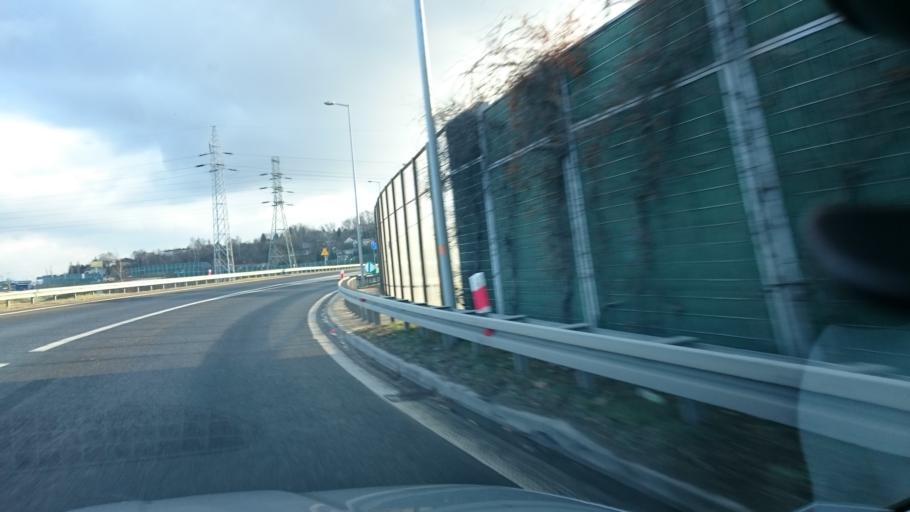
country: PL
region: Lesser Poland Voivodeship
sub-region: Powiat wielicki
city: Czarnochowice
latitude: 50.0063
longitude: 20.0168
